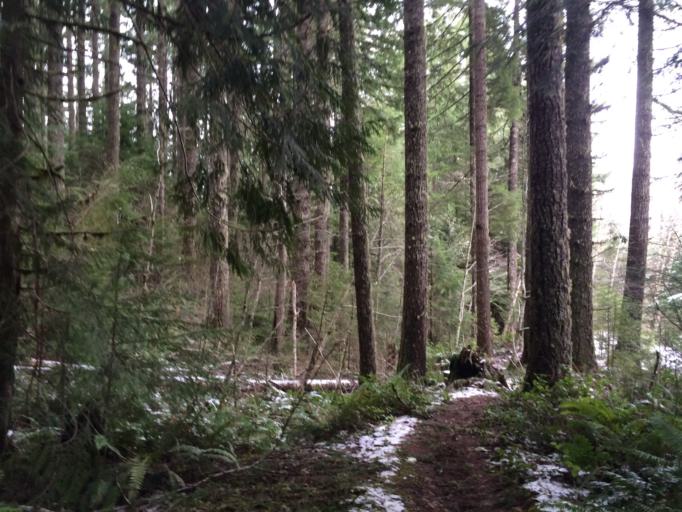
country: US
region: Oregon
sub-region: Benton County
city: Philomath
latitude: 44.5303
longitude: -123.5455
